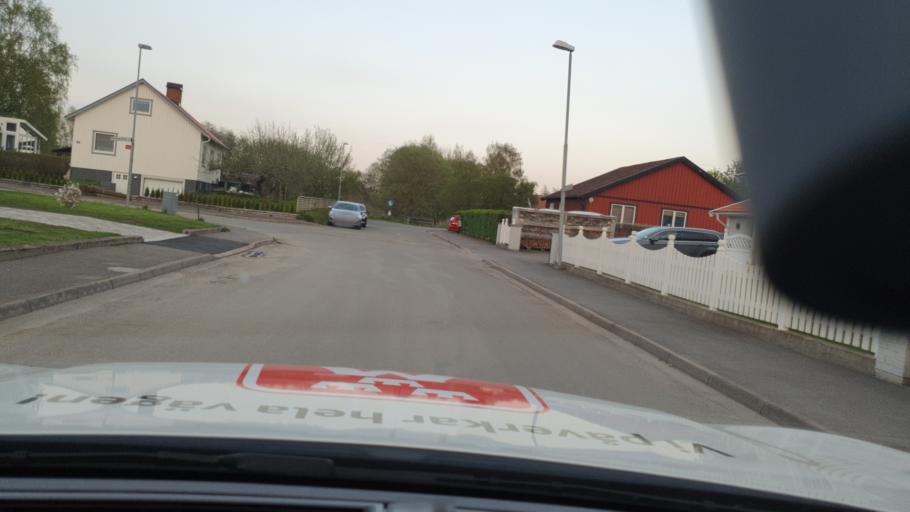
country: SE
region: Vaestra Goetaland
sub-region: Skovde Kommun
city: Skoevde
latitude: 58.3893
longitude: 13.8701
